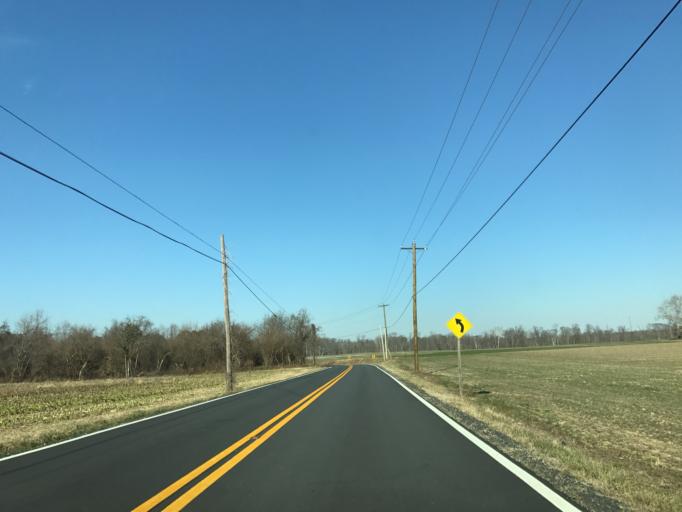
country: US
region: Maryland
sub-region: Queen Anne's County
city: Centreville
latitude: 39.0145
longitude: -76.1274
